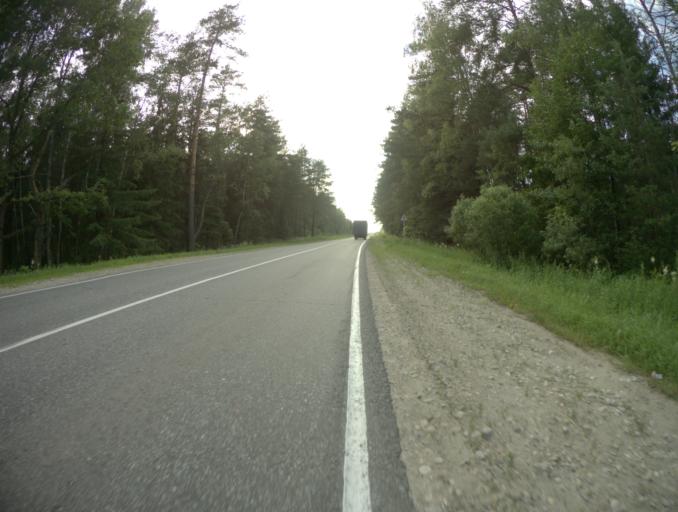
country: RU
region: Vladimir
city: Sudogda
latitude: 55.9888
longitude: 40.6894
